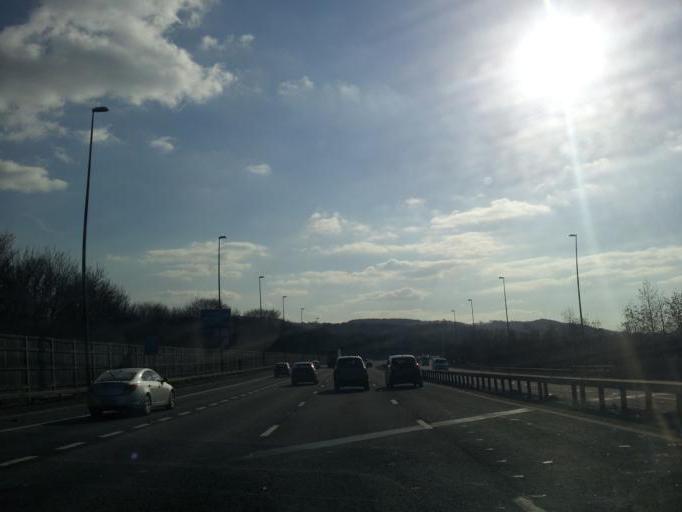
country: GB
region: England
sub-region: North Somerset
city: Easton-in-Gordano
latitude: 51.4829
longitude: -2.6996
